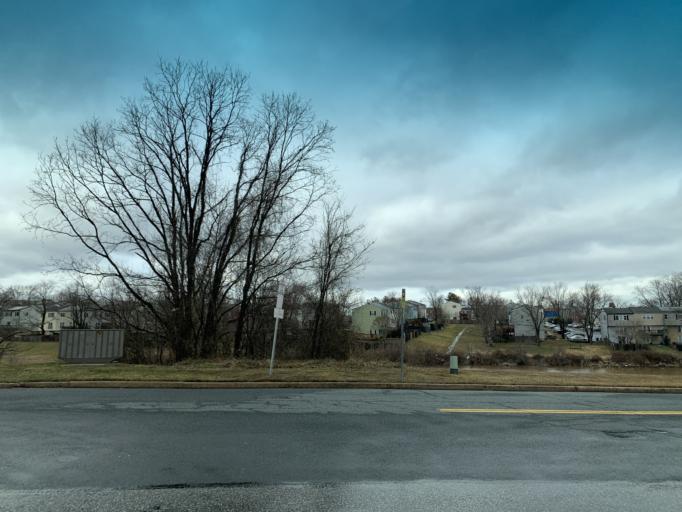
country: US
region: Maryland
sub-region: Harford County
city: Edgewood
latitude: 39.4310
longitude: -76.3136
